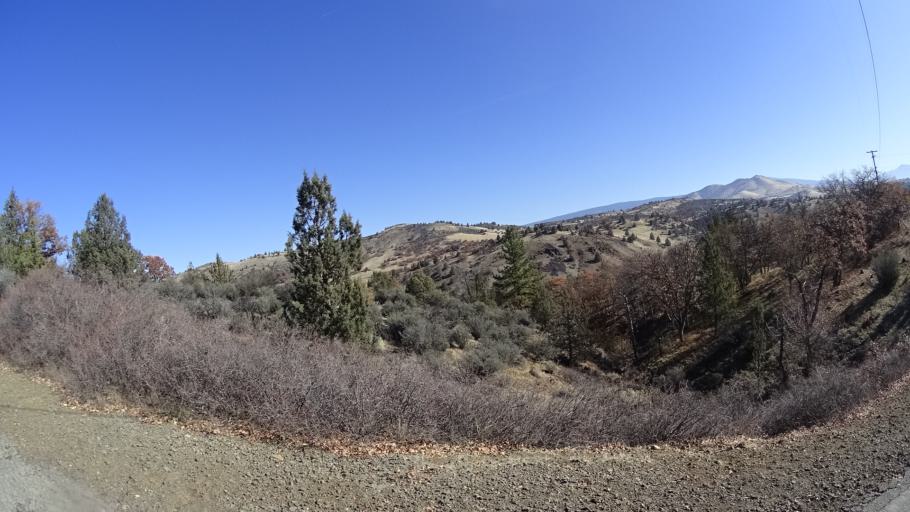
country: US
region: California
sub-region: Siskiyou County
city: Montague
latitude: 41.8752
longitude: -122.4813
